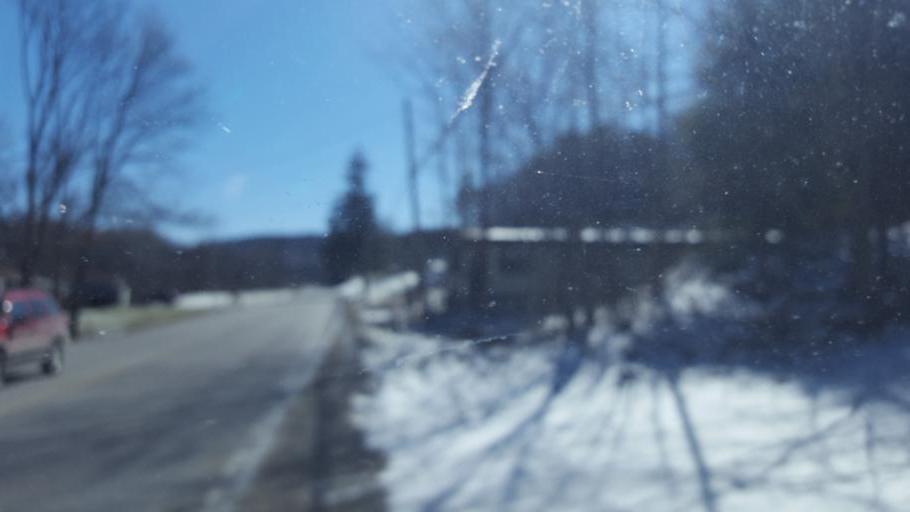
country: US
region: New York
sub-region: Allegany County
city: Wellsville
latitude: 42.0806
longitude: -77.9073
